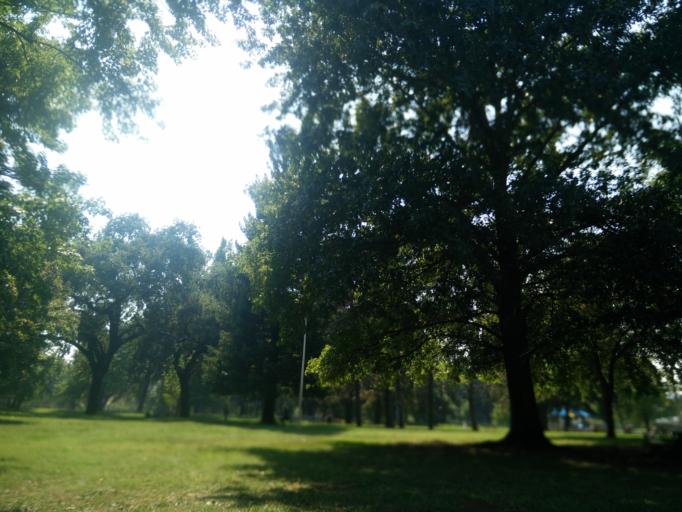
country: US
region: California
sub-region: Shasta County
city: Redding
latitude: 40.5951
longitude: -122.3912
